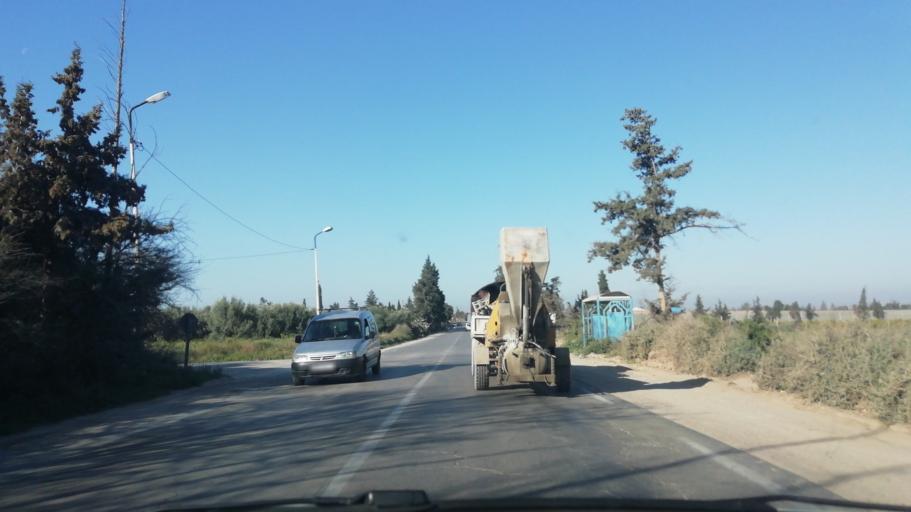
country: DZ
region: Mascara
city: Sig
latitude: 35.5657
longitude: -0.0804
